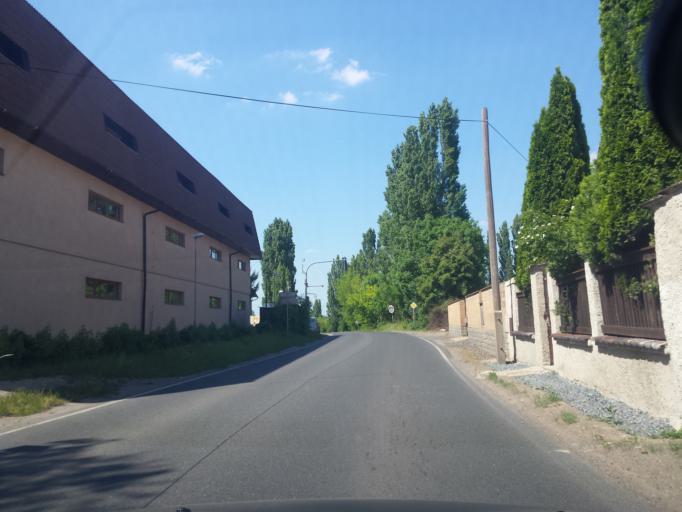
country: CZ
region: Central Bohemia
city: Horomerice
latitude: 50.1369
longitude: 14.3364
